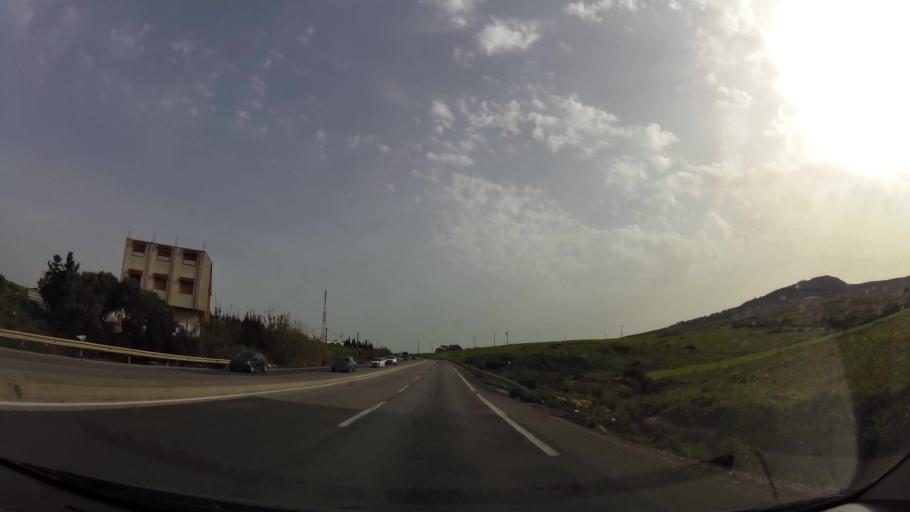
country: MA
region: Tanger-Tetouan
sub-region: Tanger-Assilah
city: Dar Chaoui
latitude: 35.6656
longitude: -5.6976
